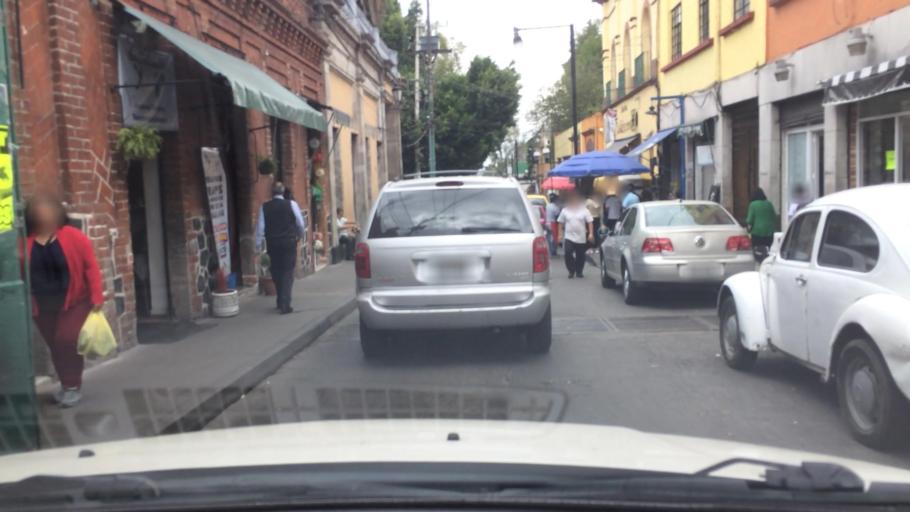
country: MX
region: Mexico City
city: Tlalpan
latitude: 19.2879
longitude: -99.1669
